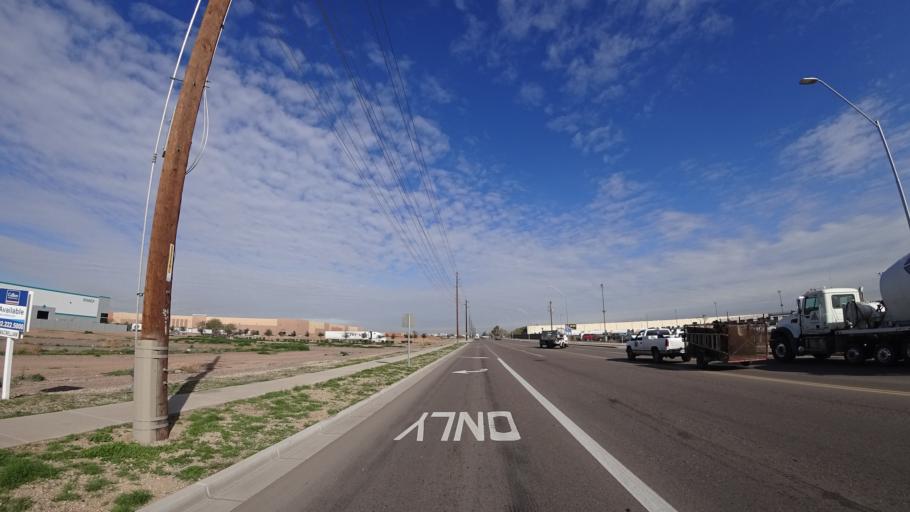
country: US
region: Arizona
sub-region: Maricopa County
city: Laveen
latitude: 33.4234
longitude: -112.1520
